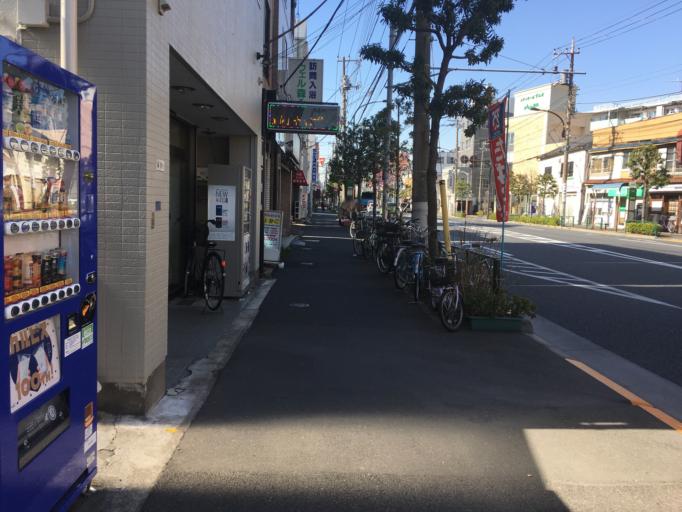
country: JP
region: Tokyo
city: Urayasu
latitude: 35.7134
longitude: 139.8270
